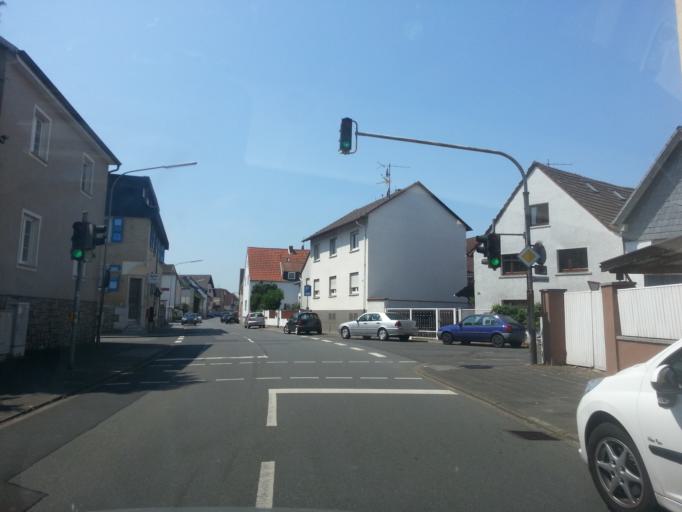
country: DE
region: Hesse
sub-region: Regierungsbezirk Darmstadt
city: Munster
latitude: 49.9270
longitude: 8.8624
